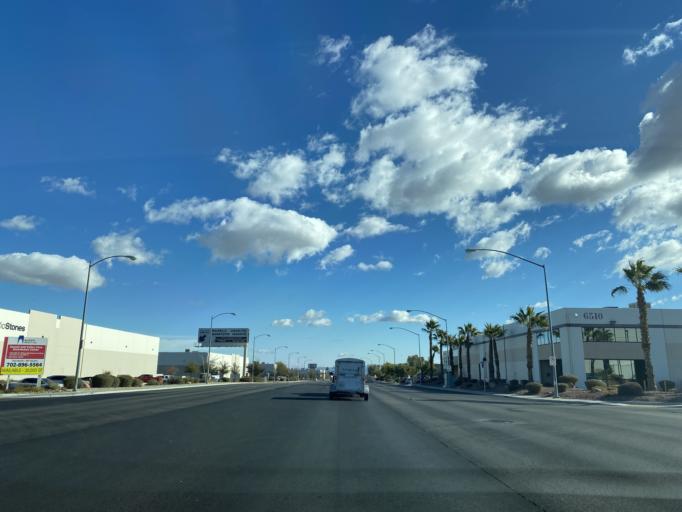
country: US
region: Nevada
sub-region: Clark County
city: Paradise
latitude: 36.0718
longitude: -115.1950
